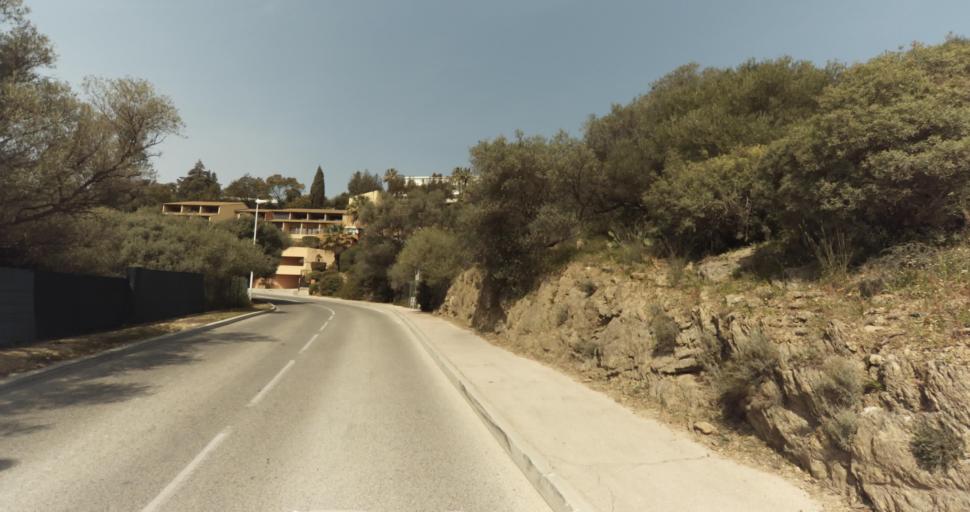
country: FR
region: Provence-Alpes-Cote d'Azur
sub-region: Departement du Var
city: Bormes-les-Mimosas
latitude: 43.1431
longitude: 6.3521
